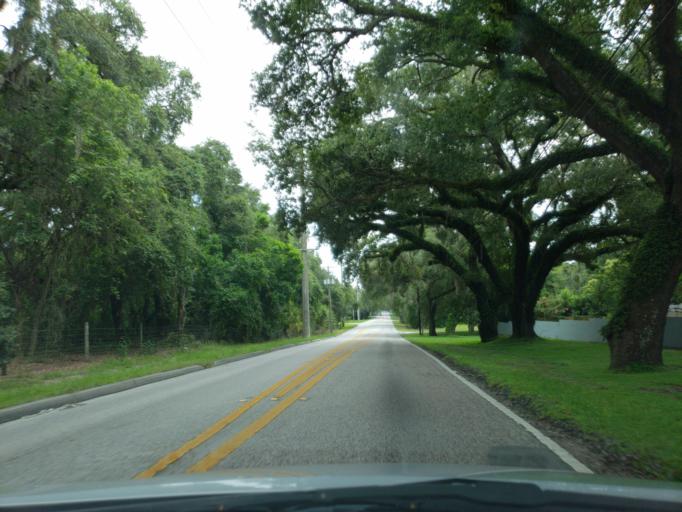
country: US
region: Florida
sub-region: Hillsborough County
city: University
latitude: 28.0967
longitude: -82.4307
